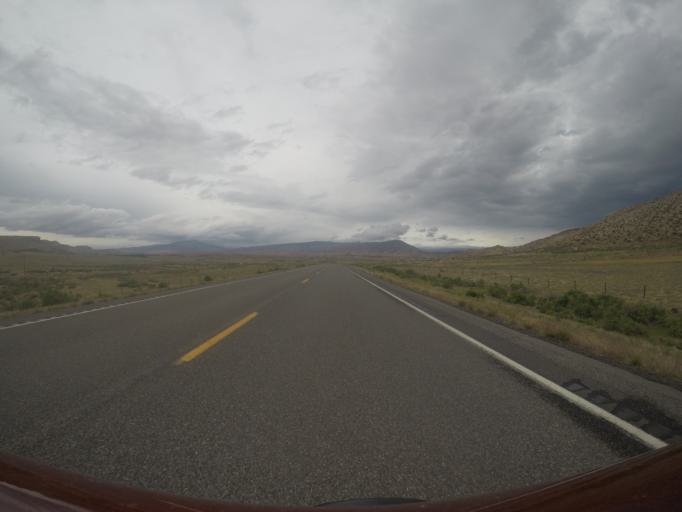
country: US
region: Wyoming
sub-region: Big Horn County
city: Lovell
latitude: 44.9420
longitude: -108.2962
